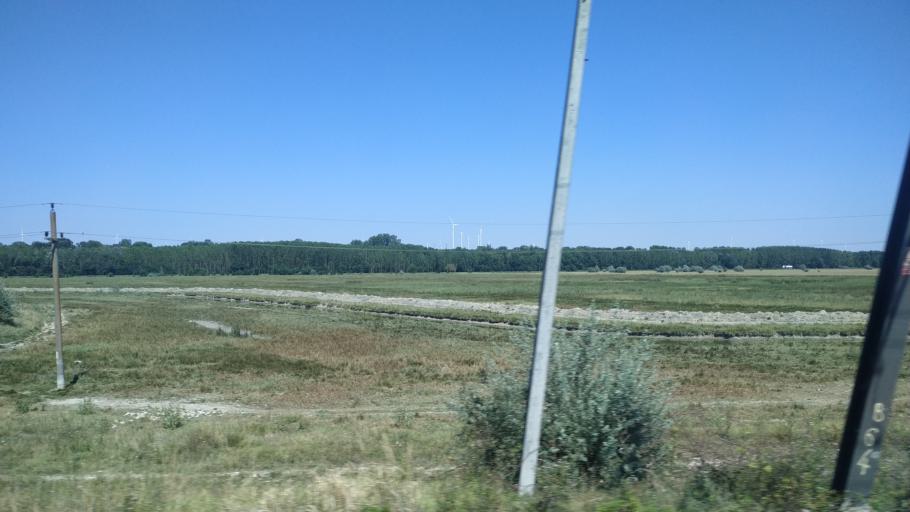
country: RO
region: Constanta
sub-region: Comuna Mircea Voda
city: Mircea Voda
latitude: 44.2648
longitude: 28.1570
